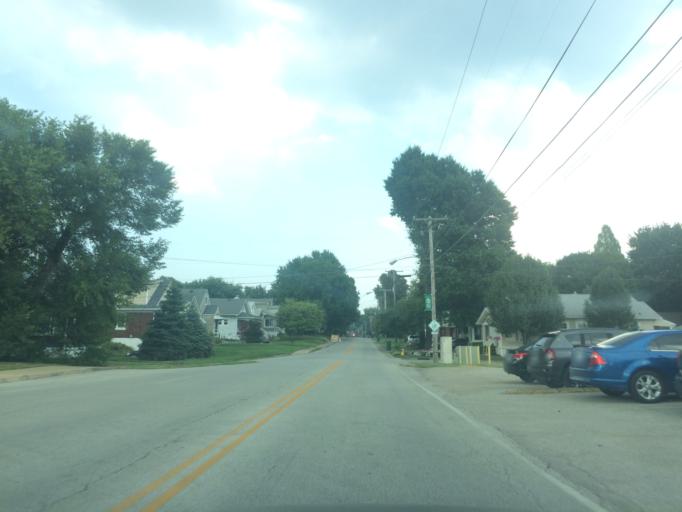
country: US
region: Kentucky
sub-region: Jefferson County
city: Audubon Park
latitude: 38.2131
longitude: -85.7412
